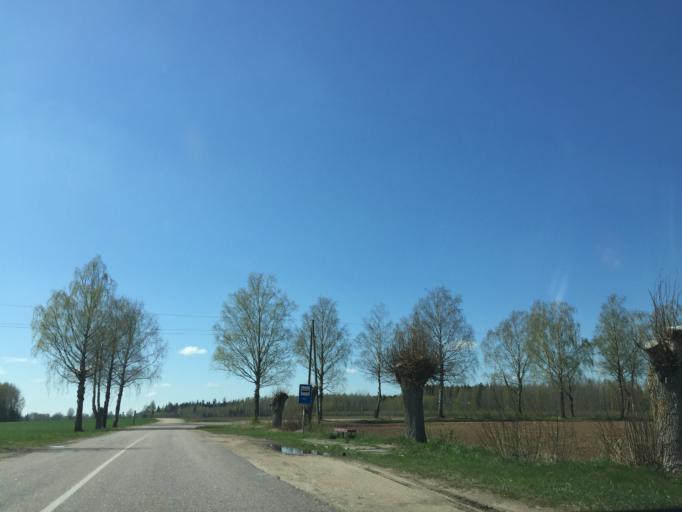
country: LV
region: Strenci
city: Seda
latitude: 57.5476
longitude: 25.8266
